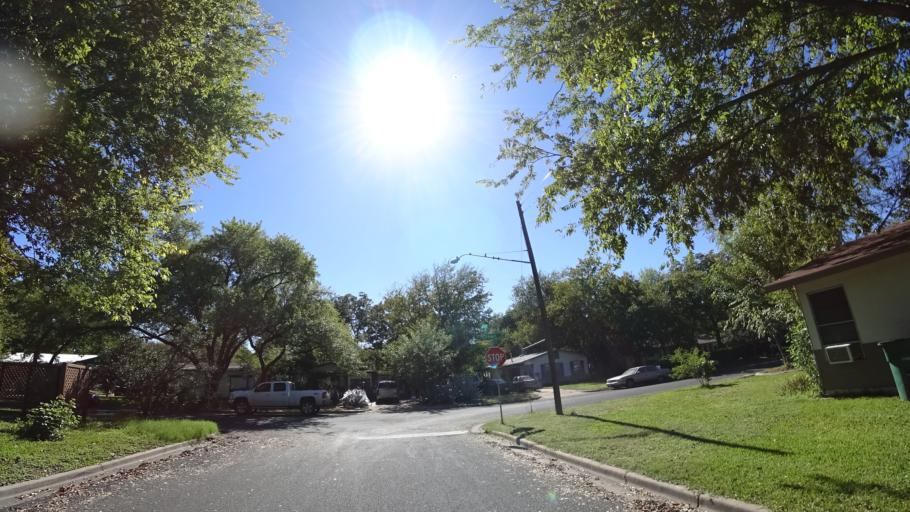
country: US
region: Texas
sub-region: Travis County
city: Rollingwood
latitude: 30.2256
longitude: -97.7880
